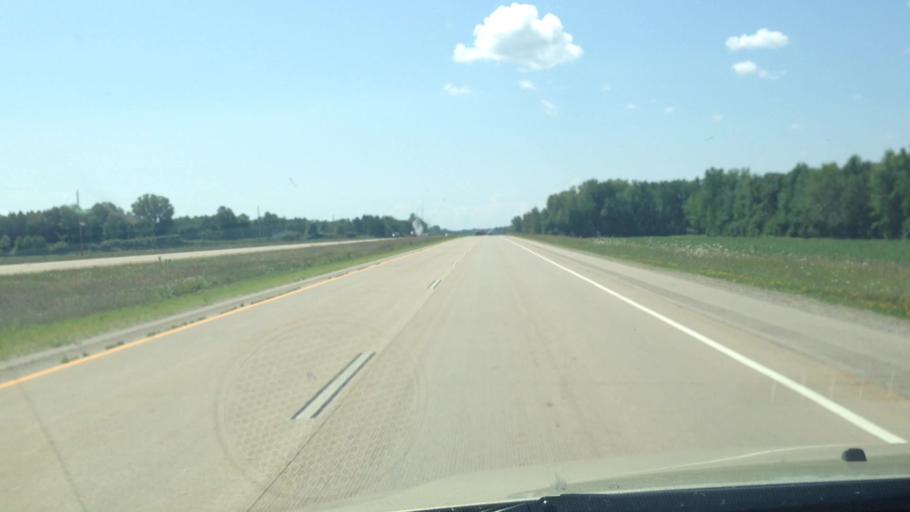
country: US
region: Wisconsin
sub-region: Oconto County
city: Oconto
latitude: 44.9549
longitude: -87.8717
